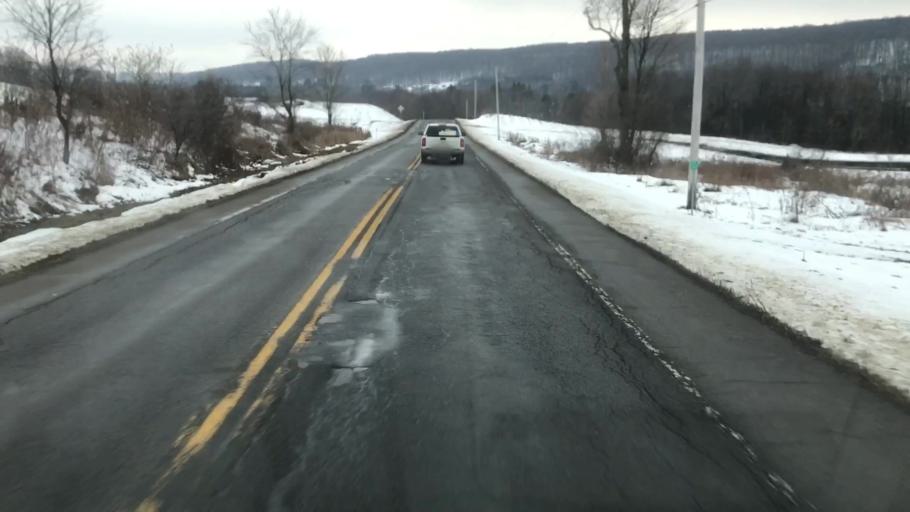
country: US
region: New York
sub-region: Tompkins County
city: Groton
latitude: 42.6863
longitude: -76.3013
